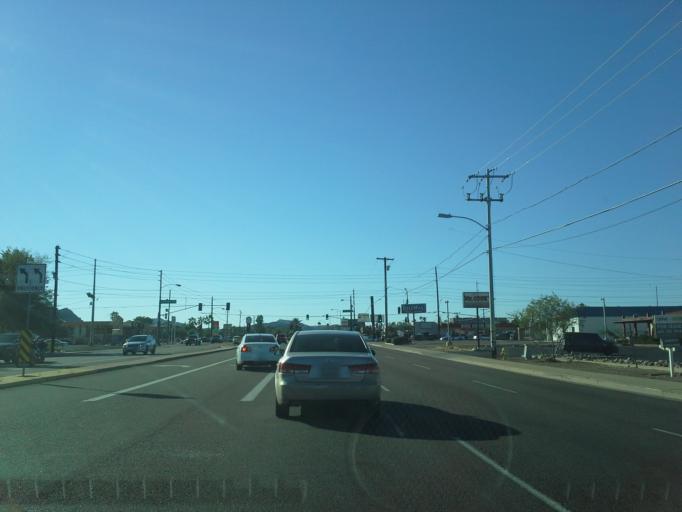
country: US
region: Arizona
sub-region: Maricopa County
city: Paradise Valley
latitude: 33.5971
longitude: -112.0117
